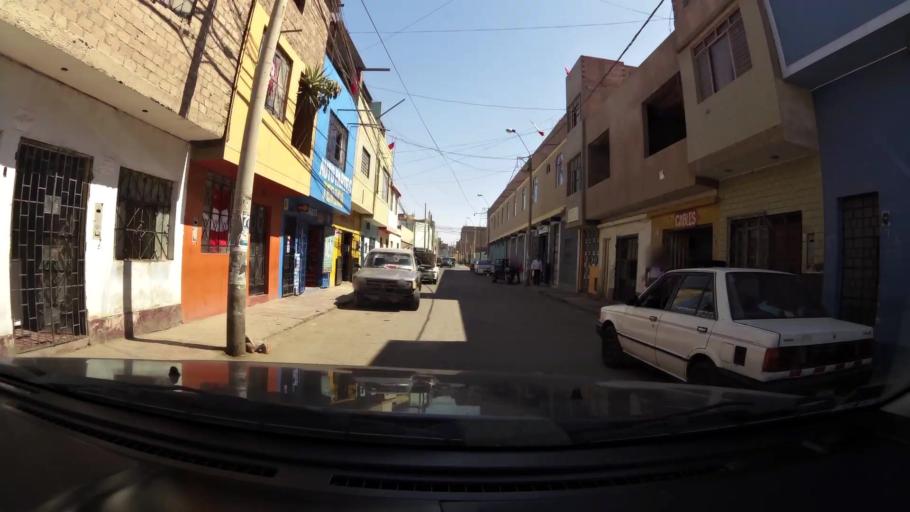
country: PE
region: Ica
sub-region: Provincia de Ica
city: Ica
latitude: -14.0676
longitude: -75.7242
